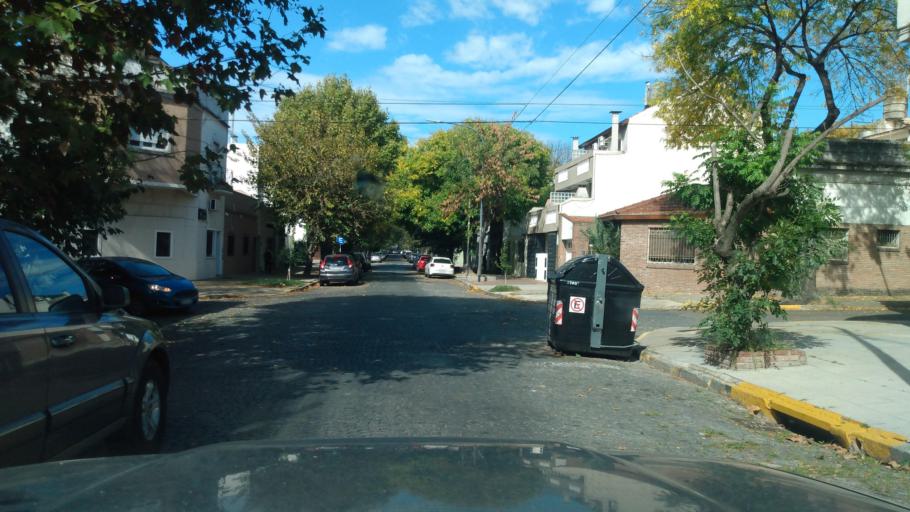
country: AR
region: Buenos Aires
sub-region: Partido de General San Martin
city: General San Martin
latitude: -34.5689
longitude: -58.4958
